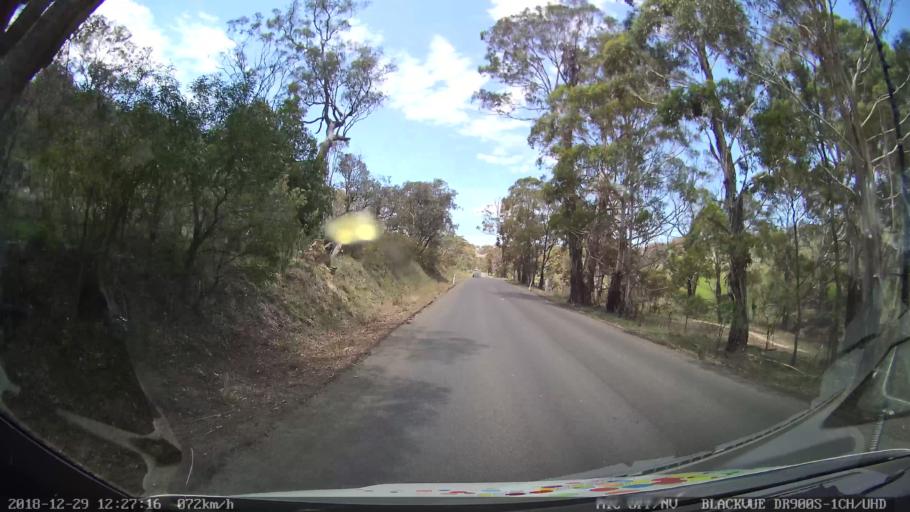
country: AU
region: Australian Capital Territory
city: Macarthur
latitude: -35.4748
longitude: 149.2231
